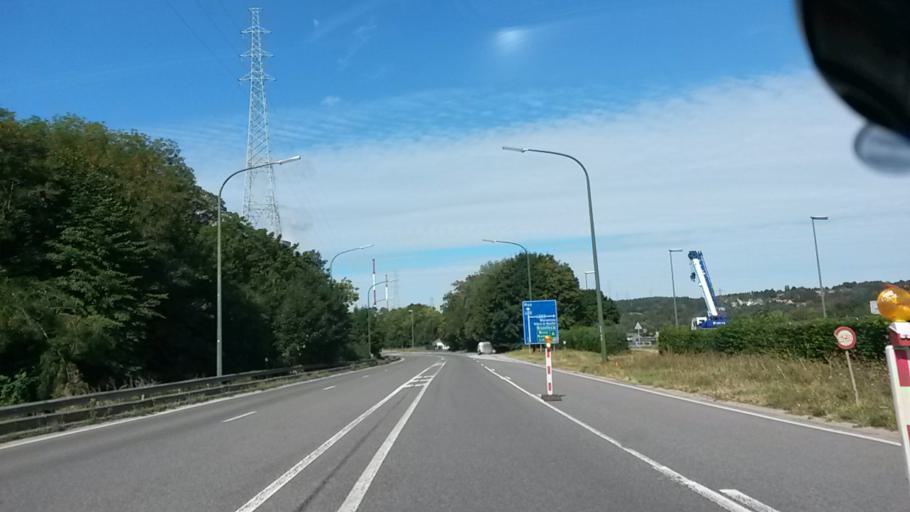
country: BE
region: Wallonia
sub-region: Province de Liege
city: Amay
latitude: 50.5322
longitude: 5.2942
